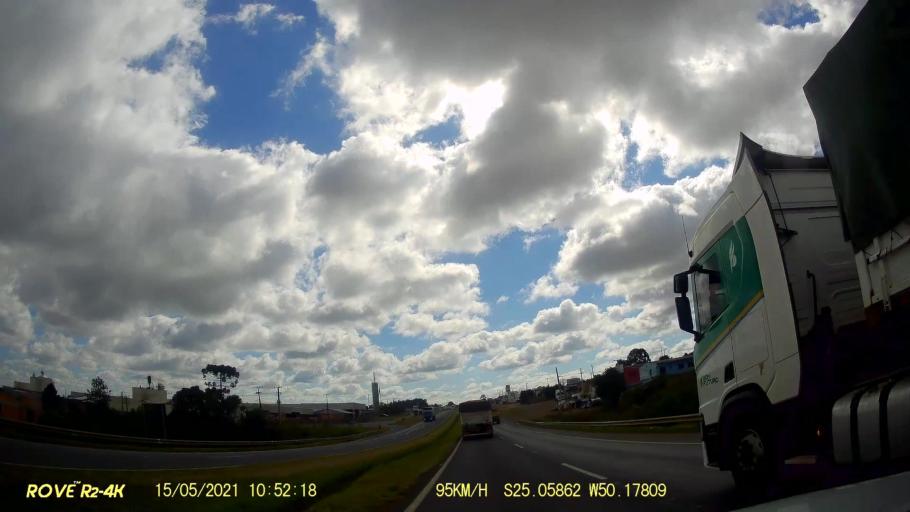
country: BR
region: Parana
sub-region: Ponta Grossa
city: Ponta Grossa
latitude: -25.0589
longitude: -50.1781
